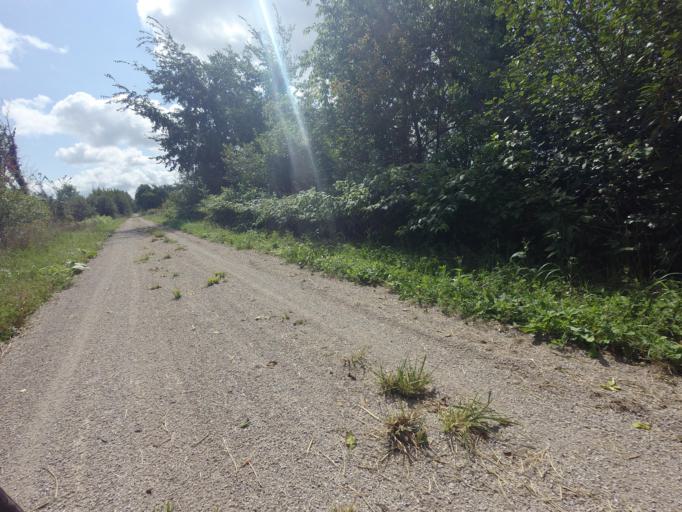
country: CA
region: Ontario
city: Huron East
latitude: 43.6506
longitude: -81.2277
